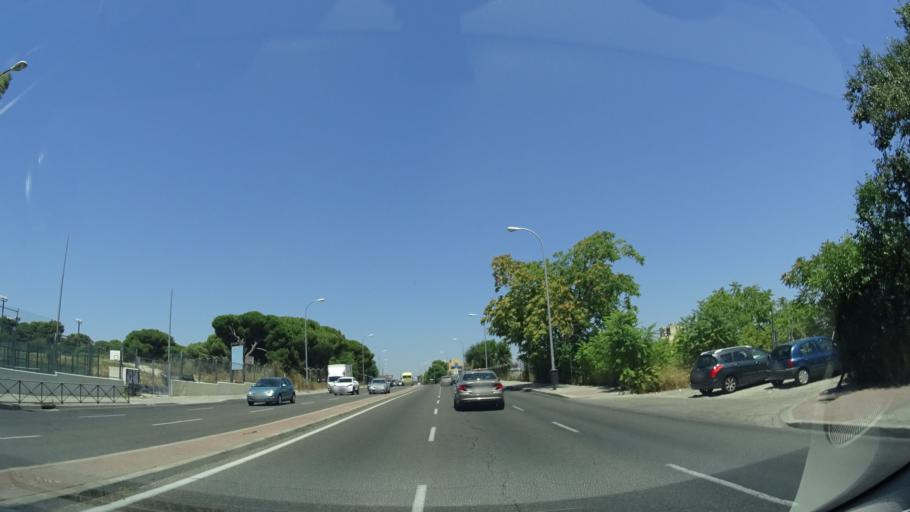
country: ES
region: Madrid
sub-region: Provincia de Madrid
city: Latina
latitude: 40.3794
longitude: -3.7562
